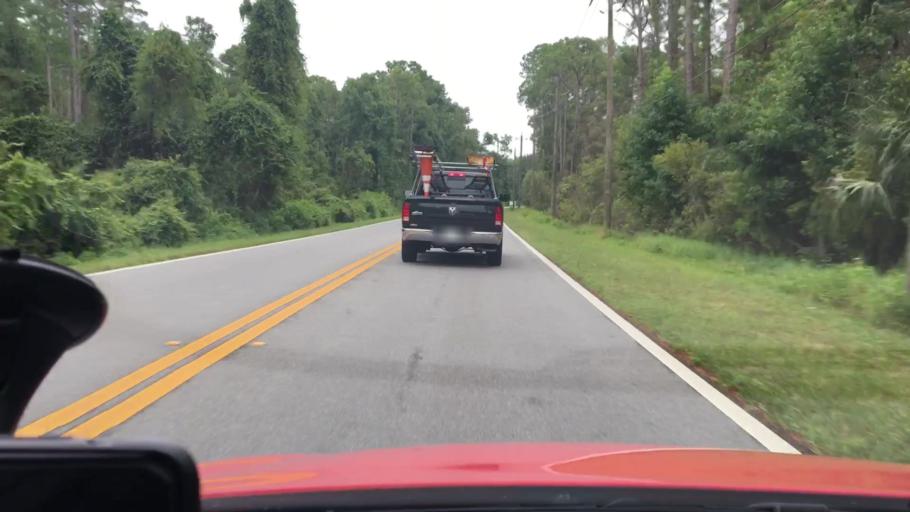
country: US
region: Florida
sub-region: Flagler County
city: Flagler Beach
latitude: 29.5081
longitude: -81.1922
